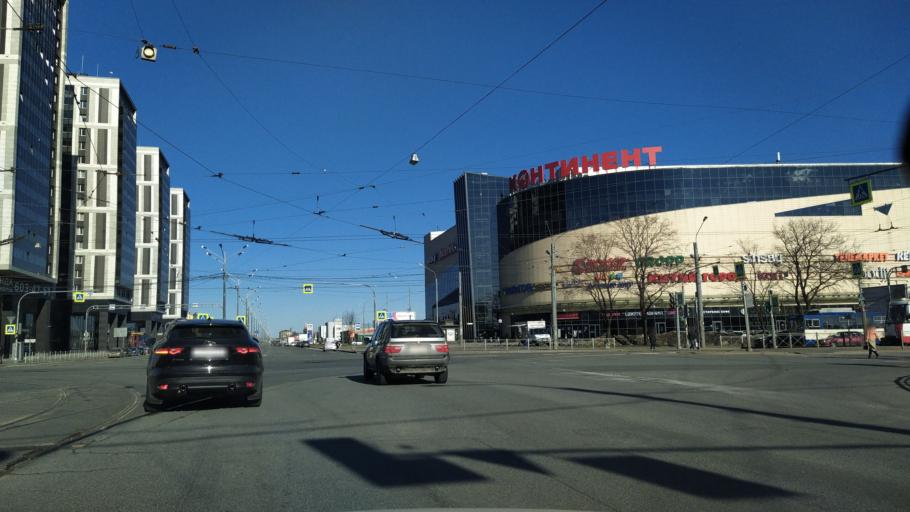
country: RU
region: St.-Petersburg
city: Kupchino
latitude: 59.8837
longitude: 30.3666
